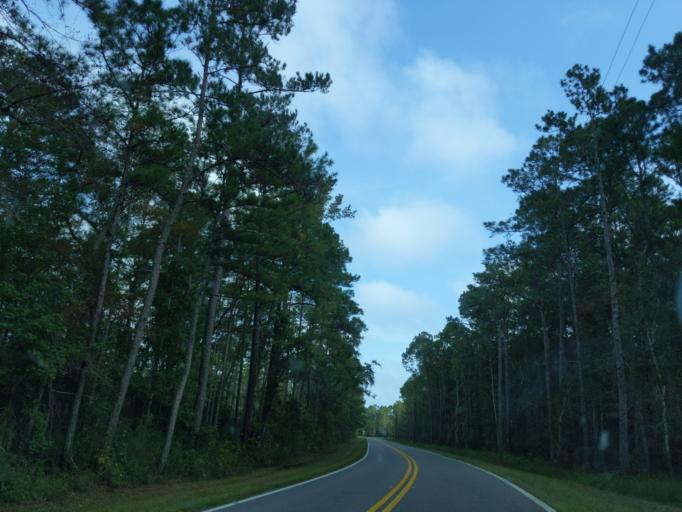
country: US
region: Florida
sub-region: Wakulla County
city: Crawfordville
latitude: 30.1048
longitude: -84.3075
